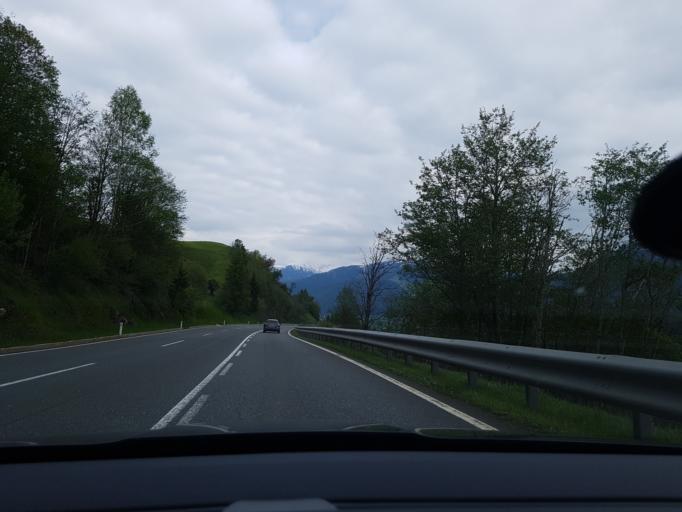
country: AT
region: Salzburg
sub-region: Politischer Bezirk Zell am See
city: Hollersbach im Pinzgau
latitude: 47.2976
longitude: 12.4230
